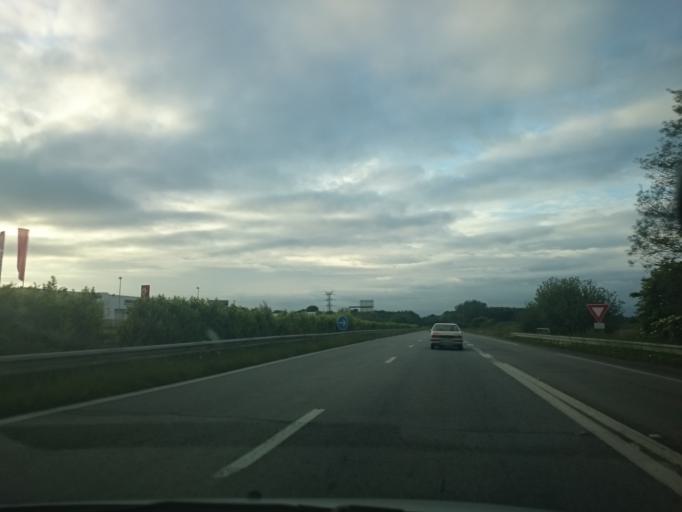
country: FR
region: Brittany
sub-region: Departement du Morbihan
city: Gestel
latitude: 47.8086
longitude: -3.4600
